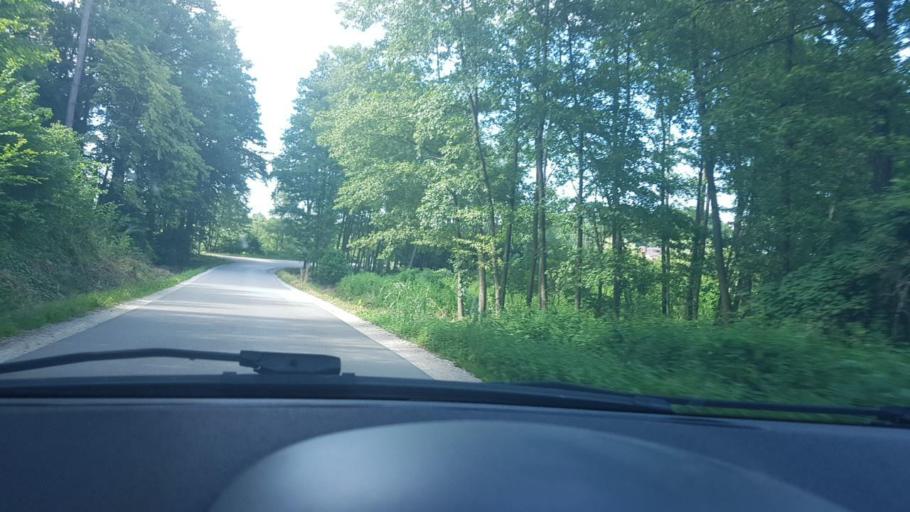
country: HR
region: Varazdinska
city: Tuzno
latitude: 46.2682
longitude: 16.1927
